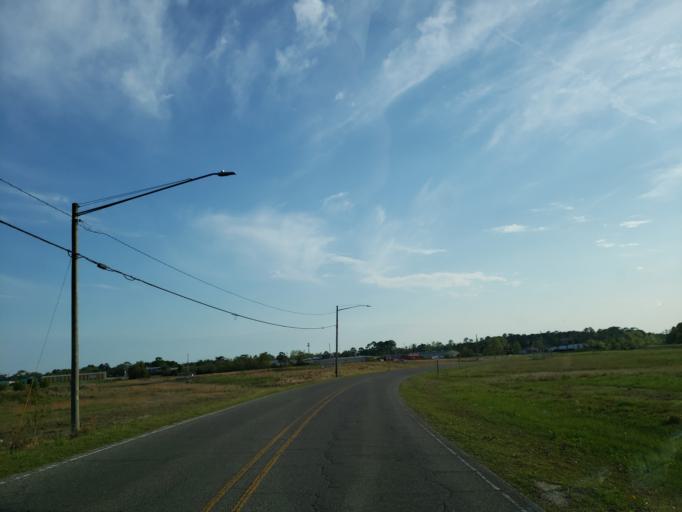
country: US
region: Mississippi
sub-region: Harrison County
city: West Gulfport
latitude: 30.3958
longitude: -89.0577
